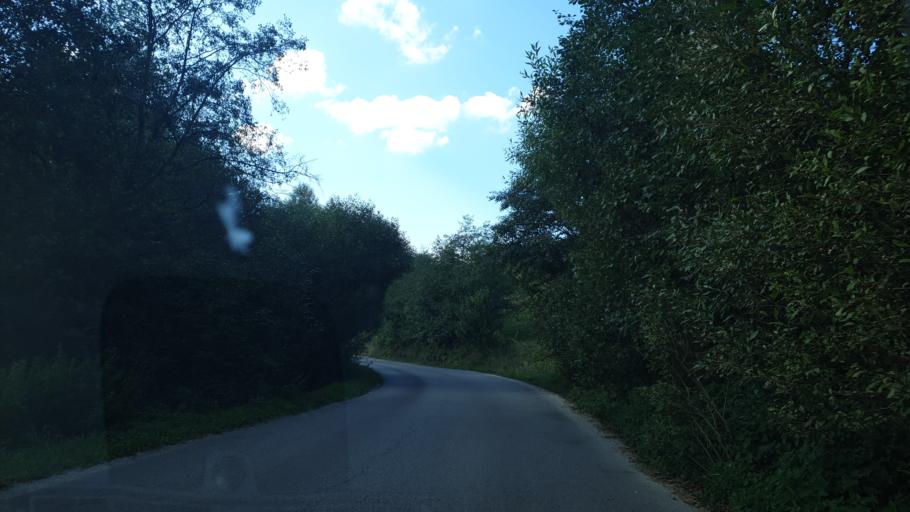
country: RS
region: Central Serbia
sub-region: Zlatiborski Okrug
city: Nova Varos
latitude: 43.4378
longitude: 19.8647
